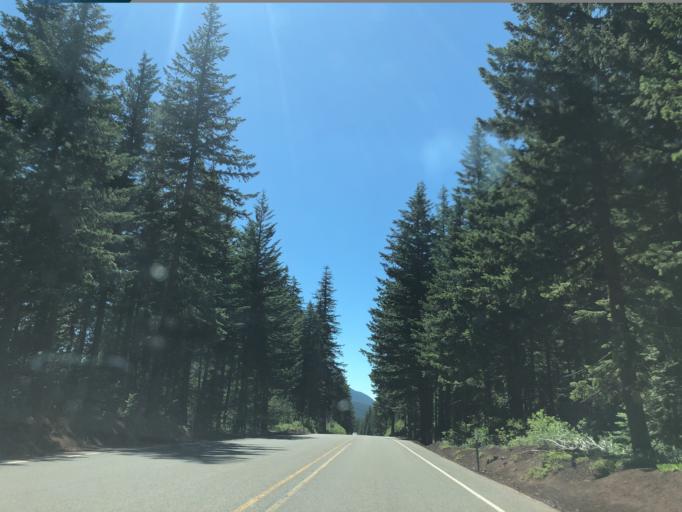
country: US
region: Oregon
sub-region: Deschutes County
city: Sisters
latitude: 44.4329
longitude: -121.9615
